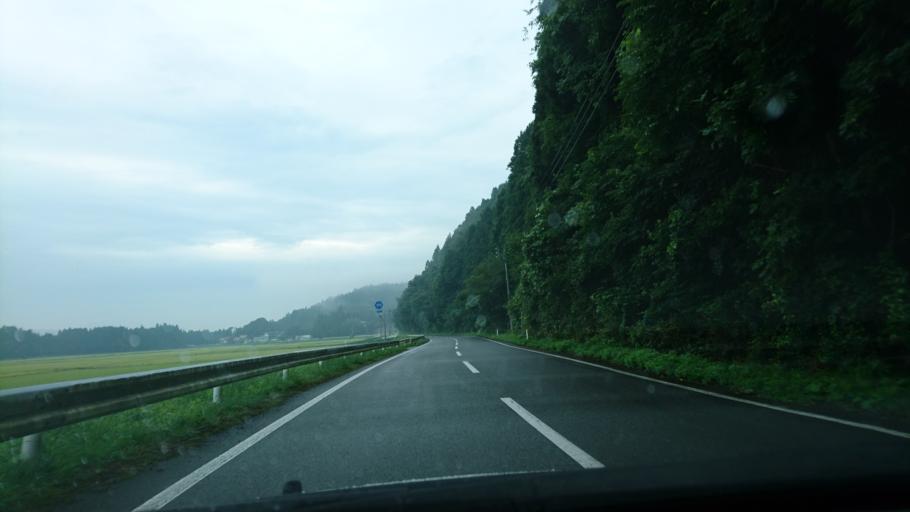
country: JP
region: Iwate
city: Ichinoseki
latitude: 38.8728
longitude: 141.2650
